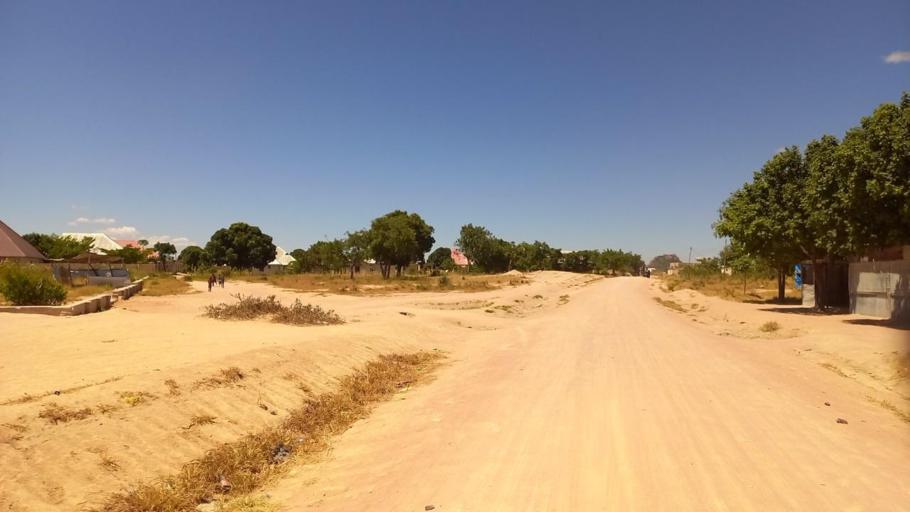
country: TZ
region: Dodoma
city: Dodoma
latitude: -6.1304
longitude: 35.7314
